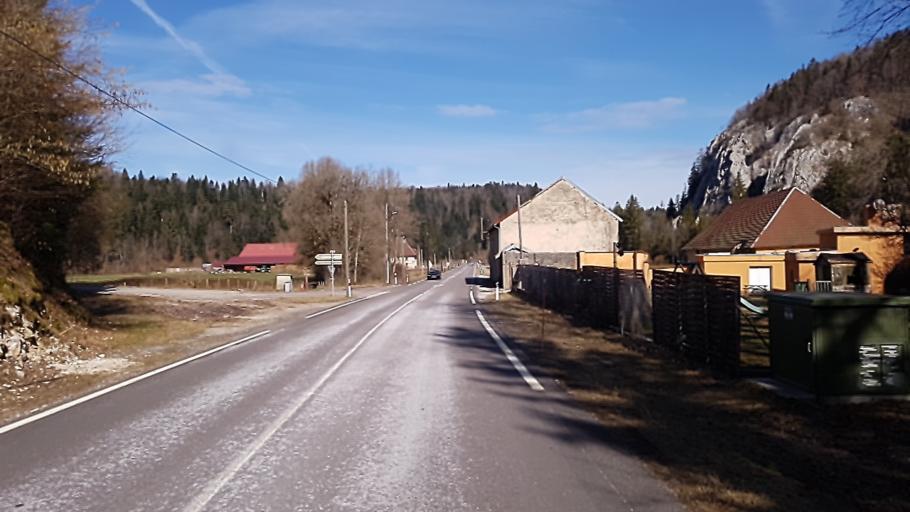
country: FR
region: Franche-Comte
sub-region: Departement du Jura
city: Champagnole
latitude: 46.6377
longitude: 5.9433
